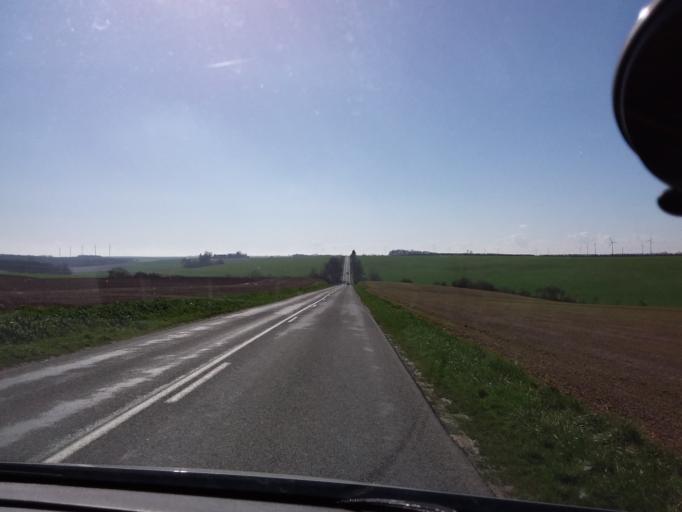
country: FR
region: Picardie
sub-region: Departement de l'Aisne
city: Montcornet
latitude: 49.6683
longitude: 4.0140
